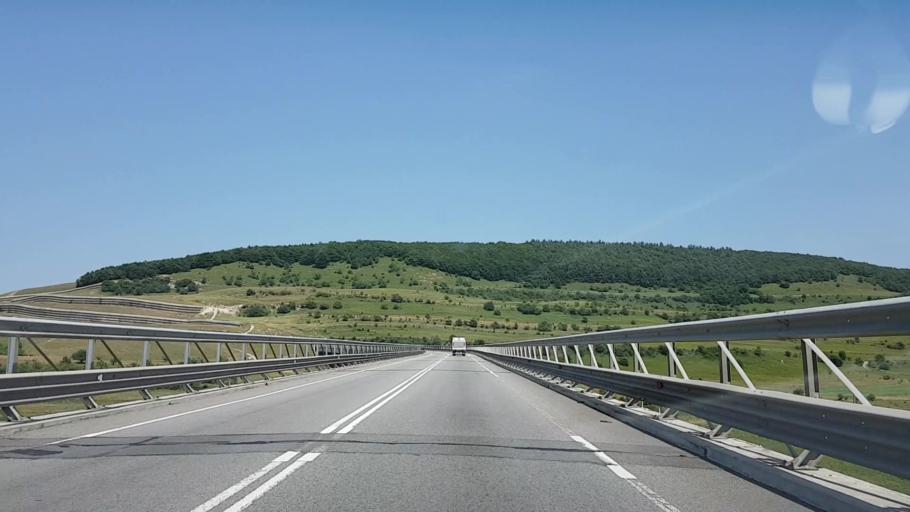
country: RO
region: Cluj
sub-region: Comuna Feleacu
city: Feleacu
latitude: 46.6896
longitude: 23.6322
